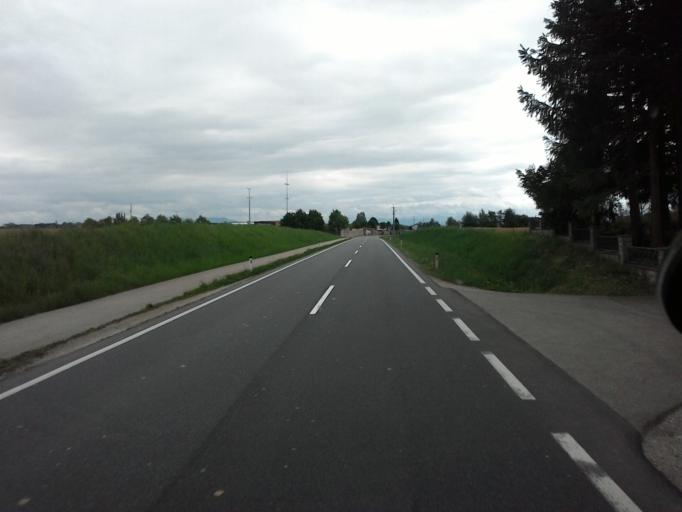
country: AT
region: Upper Austria
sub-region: Wels-Land
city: Sattledt
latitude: 48.0570
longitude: 14.0537
